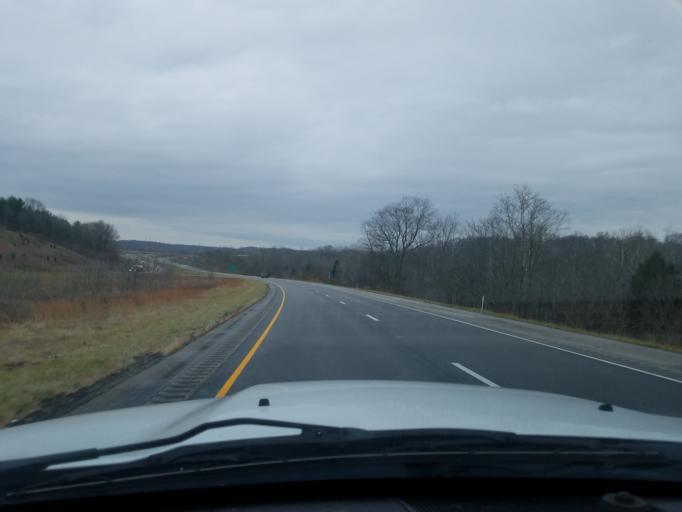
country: US
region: Indiana
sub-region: Dubois County
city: Ferdinand
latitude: 38.2305
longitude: -86.6889
